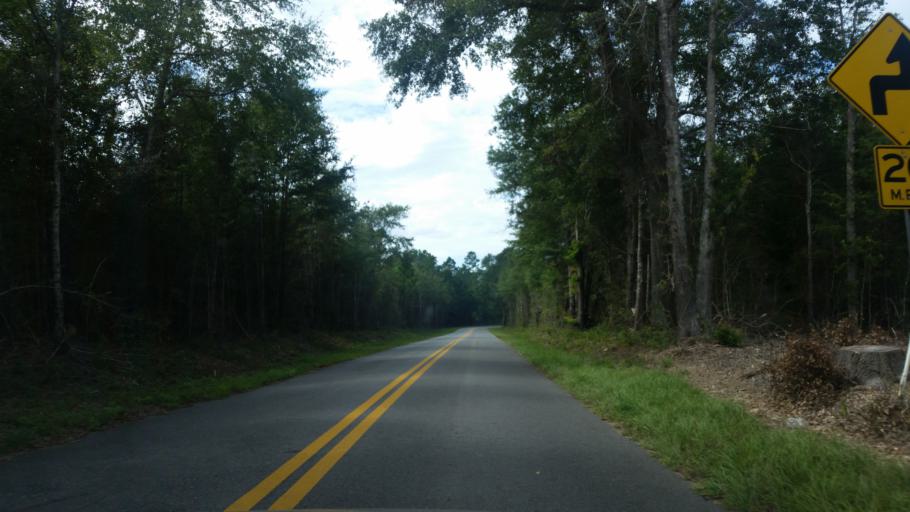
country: US
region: Florida
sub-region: Santa Rosa County
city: Point Baker
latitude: 30.7325
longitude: -87.0101
